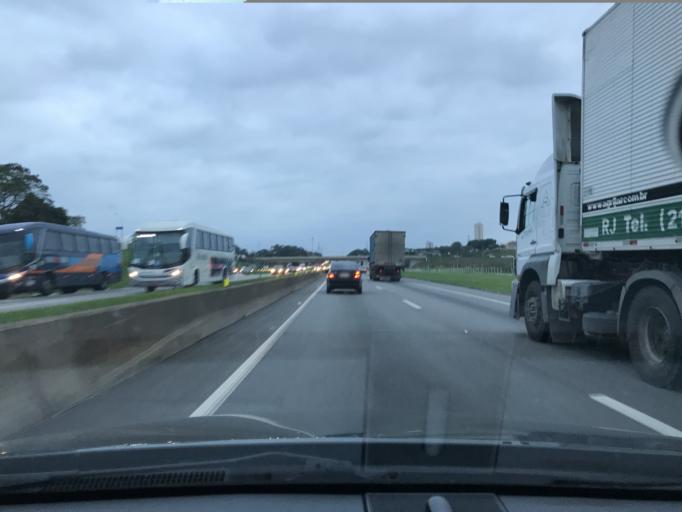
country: BR
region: Sao Paulo
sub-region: Sao Jose Dos Campos
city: Sao Jose dos Campos
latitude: -23.1777
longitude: -45.8360
